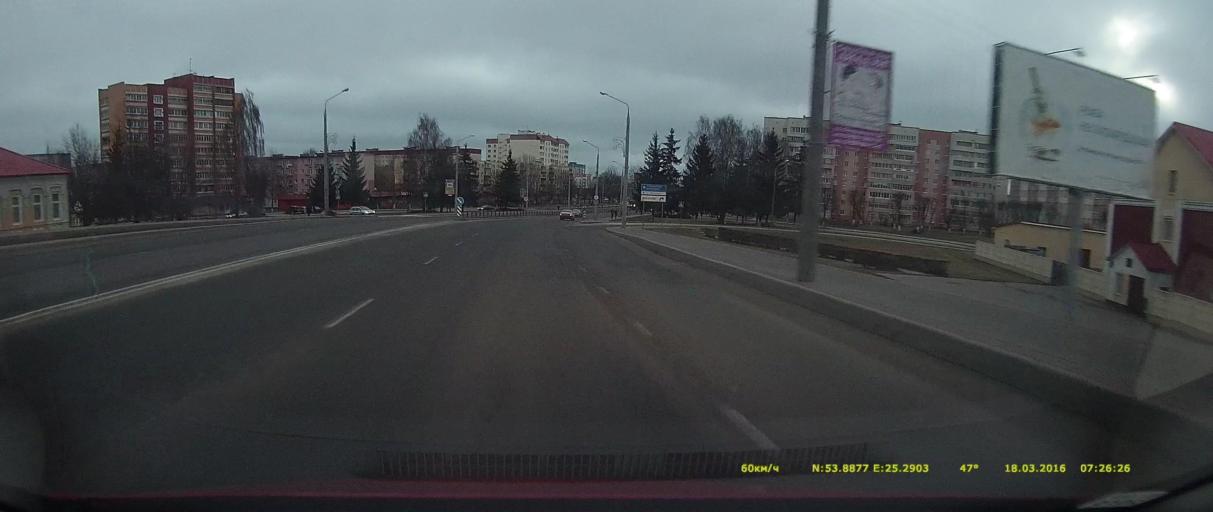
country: BY
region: Grodnenskaya
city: Lida
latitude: 53.8878
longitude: 25.2906
